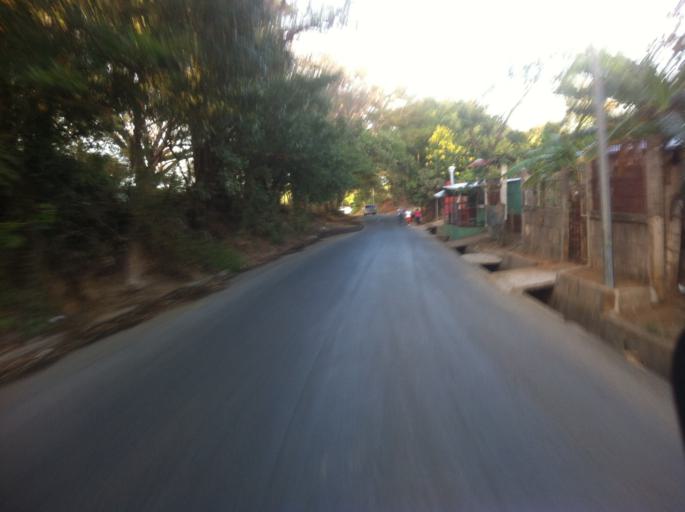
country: NI
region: Managua
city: Managua
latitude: 12.1040
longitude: -86.3015
